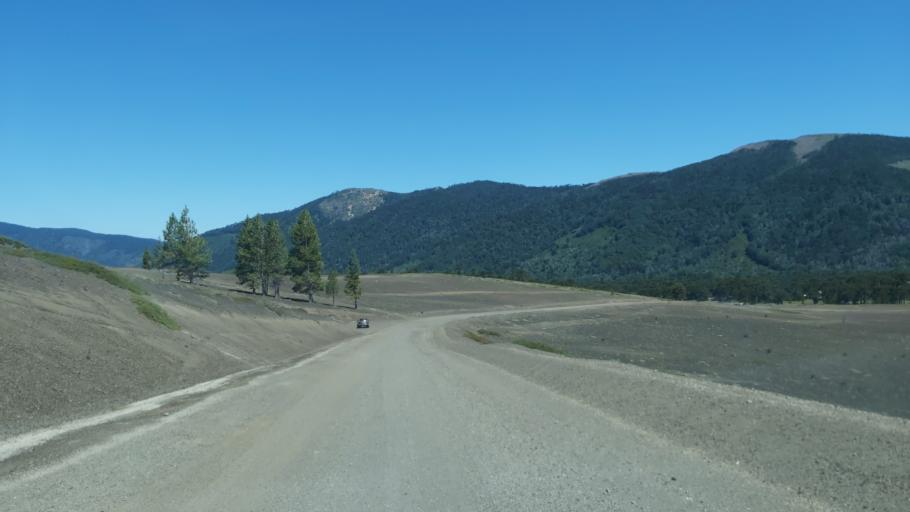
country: CL
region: Araucania
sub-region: Provincia de Cautin
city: Vilcun
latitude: -38.4134
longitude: -71.5419
